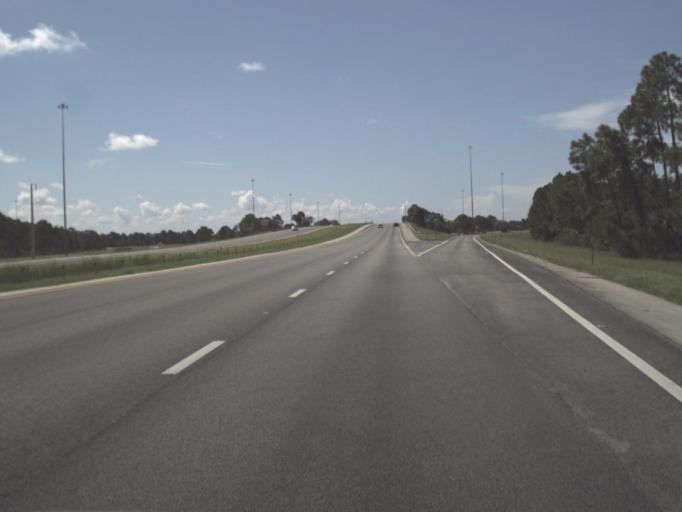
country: US
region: Florida
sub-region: Charlotte County
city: Charlotte Park
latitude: 26.8632
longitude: -81.9723
